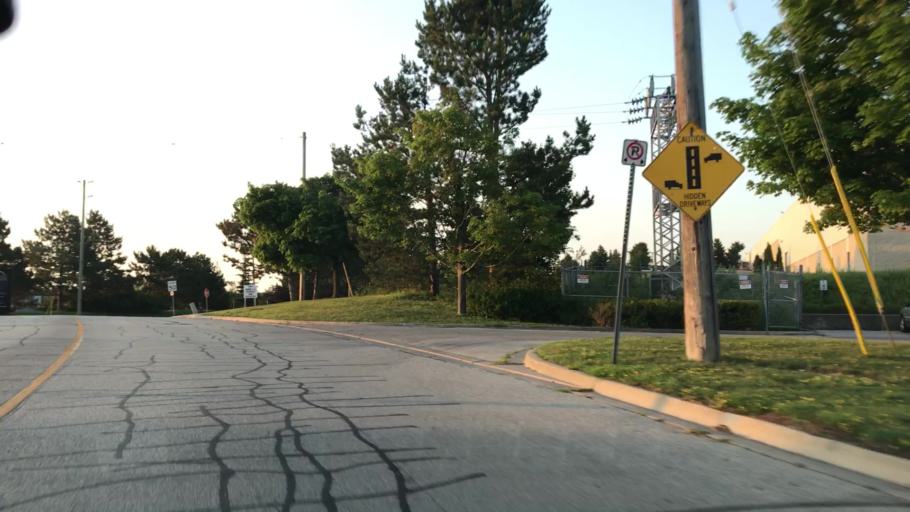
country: CA
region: Ontario
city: Newmarket
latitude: 44.0127
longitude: -79.4624
